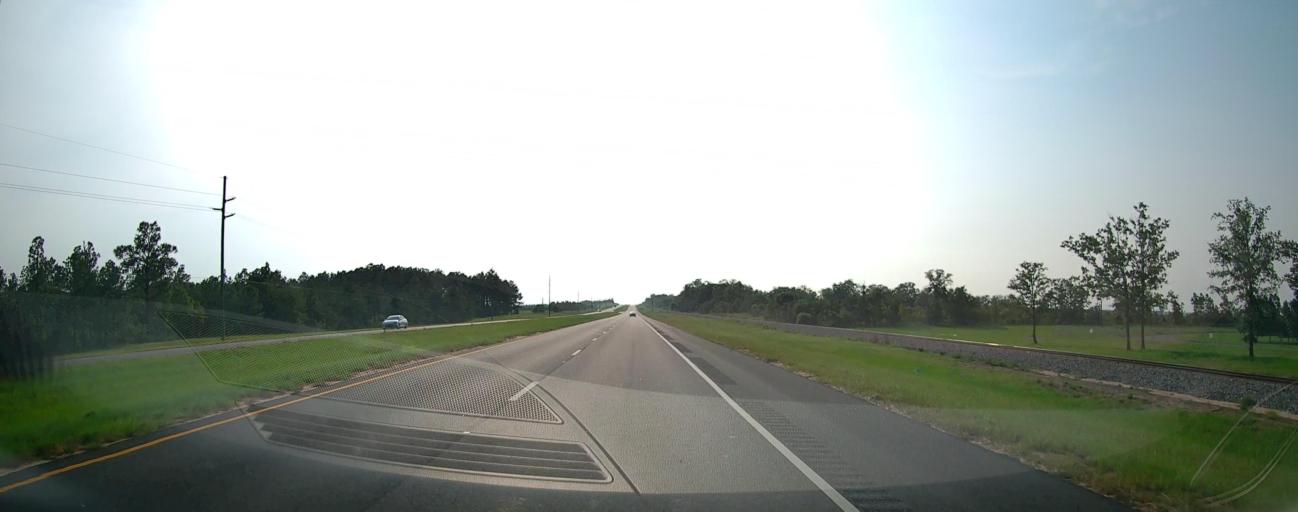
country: US
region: Georgia
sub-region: Taylor County
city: Butler
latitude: 32.5750
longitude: -84.3010
